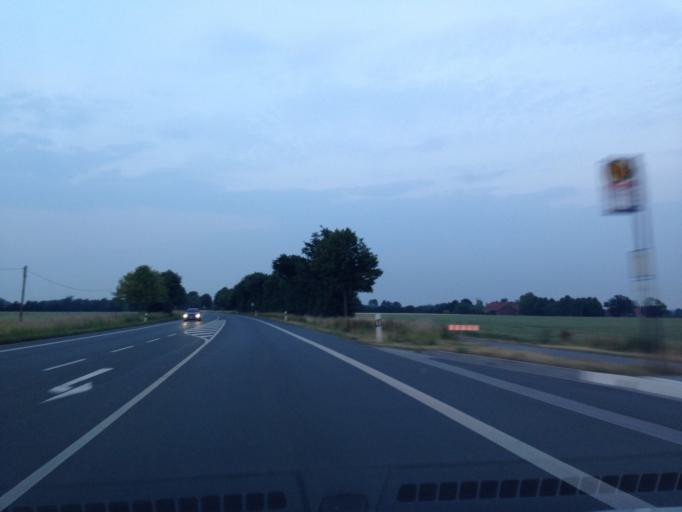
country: DE
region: North Rhine-Westphalia
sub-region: Regierungsbezirk Munster
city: Nordkirchen
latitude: 51.7869
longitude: 7.5428
